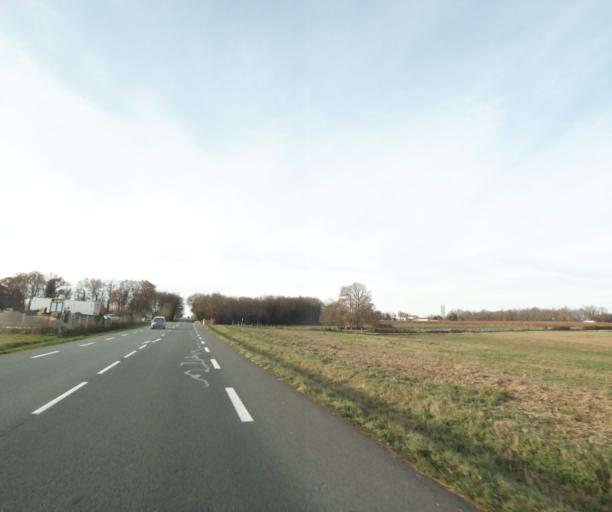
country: FR
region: Poitou-Charentes
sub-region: Departement de la Charente-Maritime
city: Chaniers
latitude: 45.7429
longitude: -0.5539
